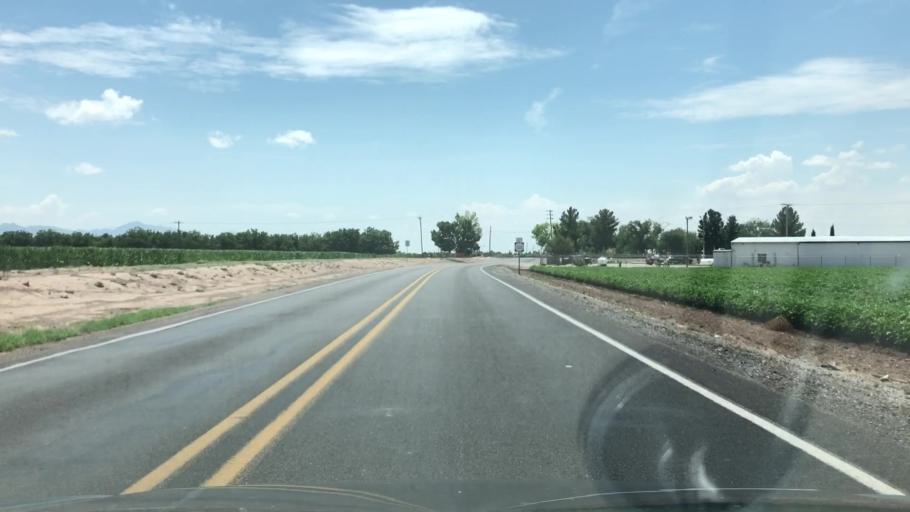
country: US
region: New Mexico
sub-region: Dona Ana County
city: Vado
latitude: 32.0633
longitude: -106.6782
